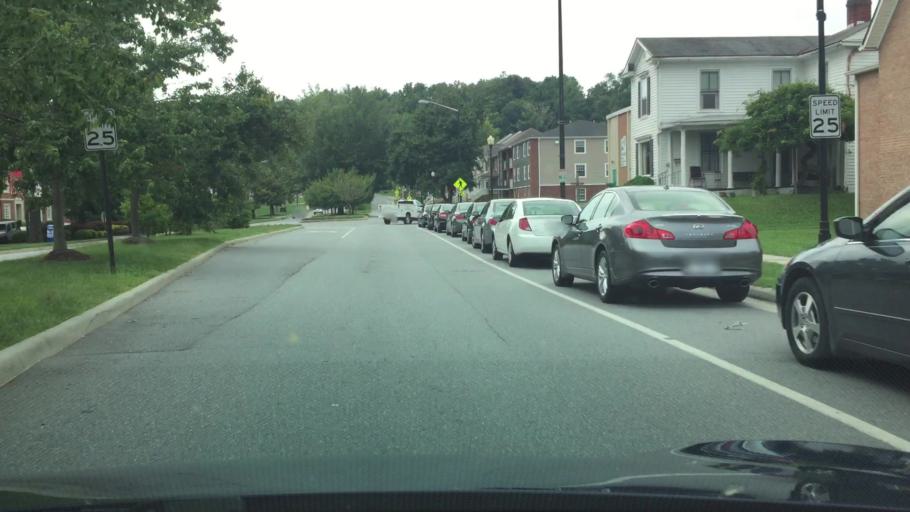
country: US
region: Virginia
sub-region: City of Radford
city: Radford
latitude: 37.1374
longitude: -80.5531
